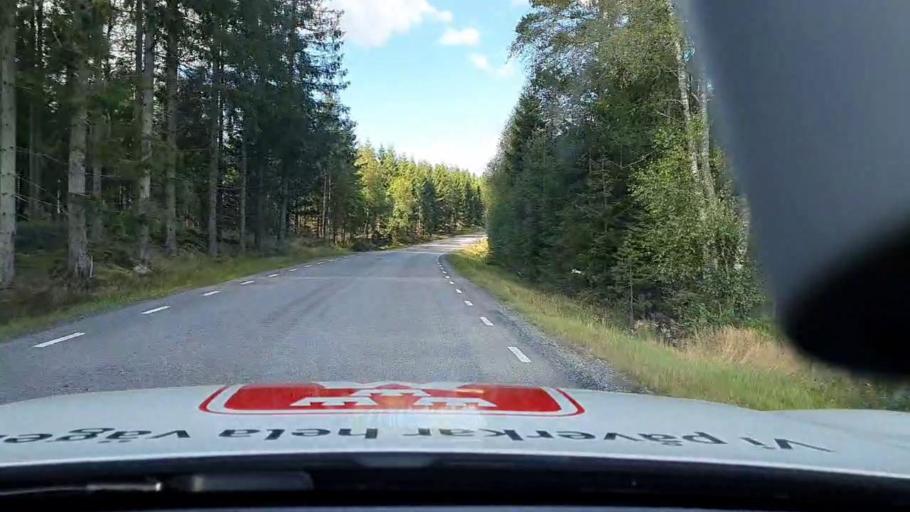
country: SE
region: Vaestra Goetaland
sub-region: Marks Kommun
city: Fritsla
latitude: 57.3687
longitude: 12.8632
